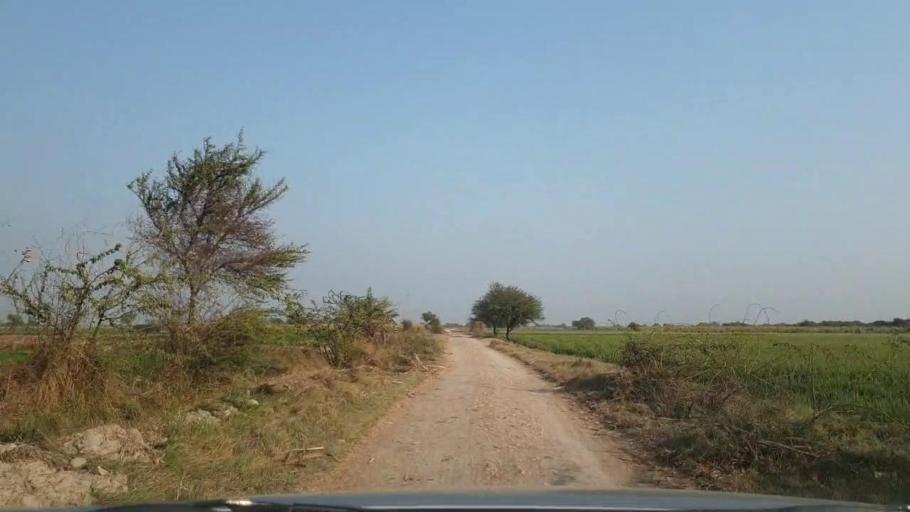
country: PK
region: Sindh
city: Tando Adam
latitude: 25.6716
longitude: 68.6378
